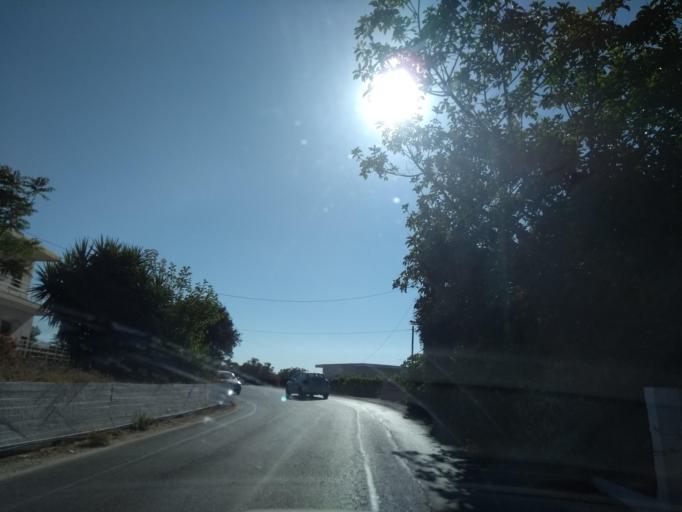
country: GR
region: Crete
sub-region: Nomos Chanias
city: Pithari
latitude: 35.5601
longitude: 24.0913
